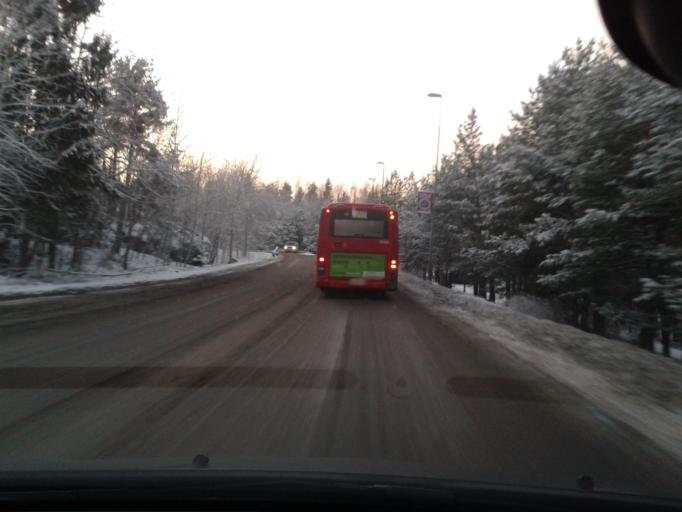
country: SE
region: Stockholm
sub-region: Haninge Kommun
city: Haninge
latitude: 59.1733
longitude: 18.1638
